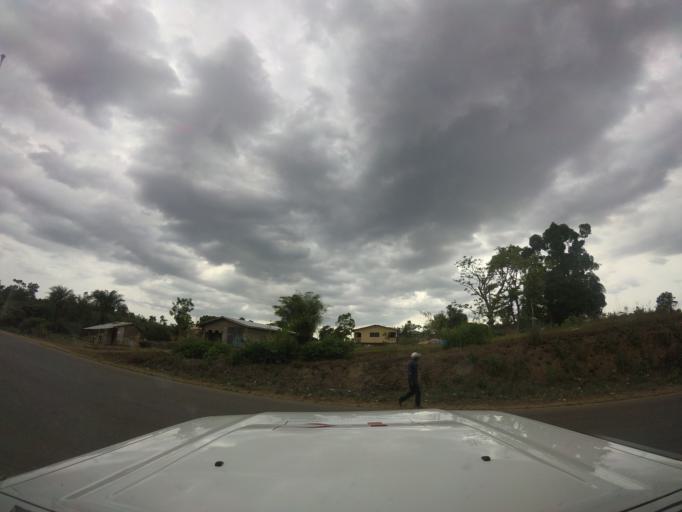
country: LR
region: Bomi
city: Tubmanburg
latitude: 6.8590
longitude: -10.8179
